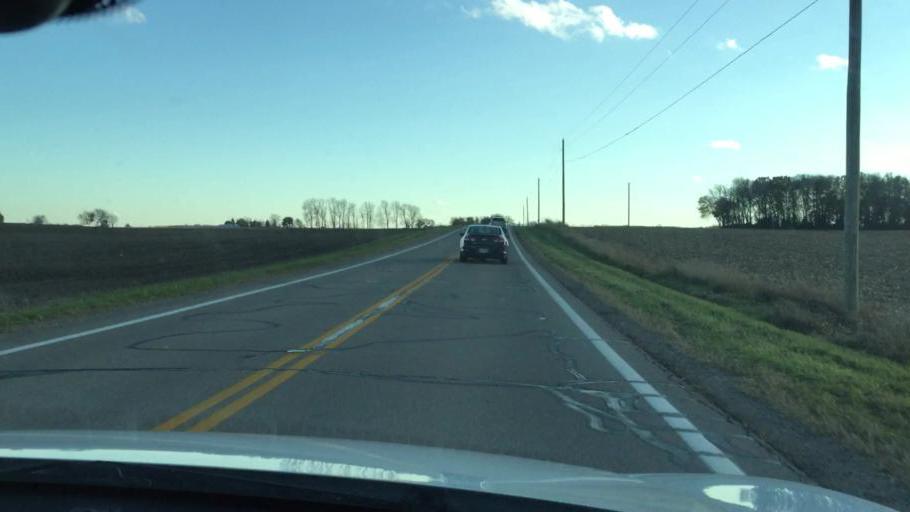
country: US
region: Ohio
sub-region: Champaign County
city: North Lewisburg
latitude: 40.1591
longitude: -83.5274
